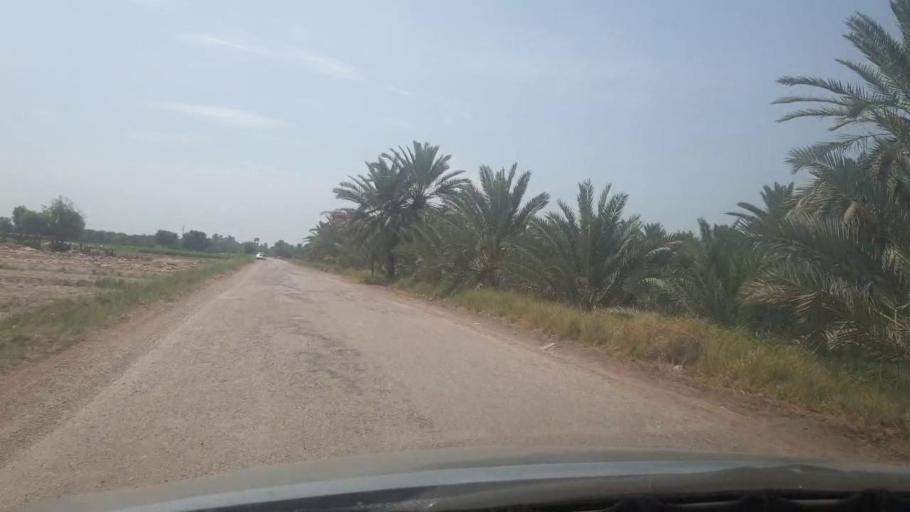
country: PK
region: Sindh
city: Bozdar
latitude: 27.2048
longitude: 68.5808
